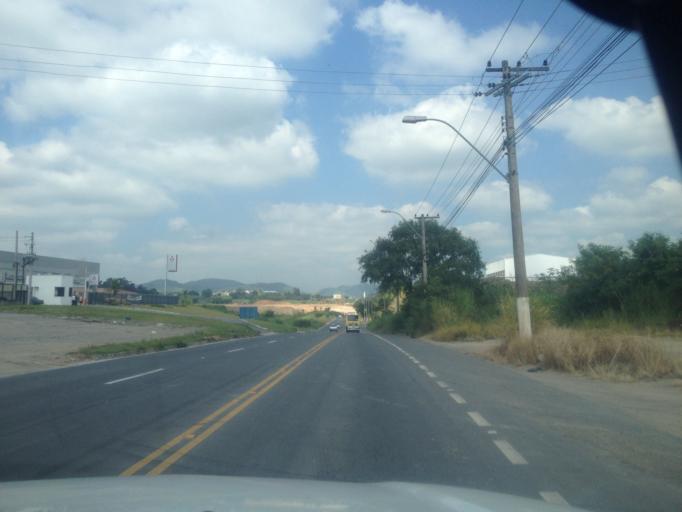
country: BR
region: Rio de Janeiro
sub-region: Volta Redonda
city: Volta Redonda
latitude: -22.5795
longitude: -44.0768
